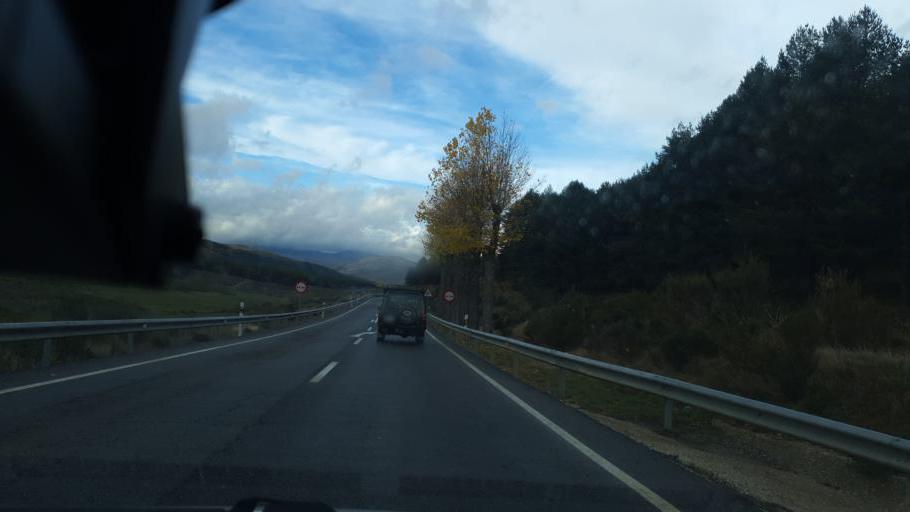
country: ES
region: Castille and Leon
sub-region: Provincia de Avila
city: Cuevas del Valle
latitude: 40.3326
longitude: -5.0127
